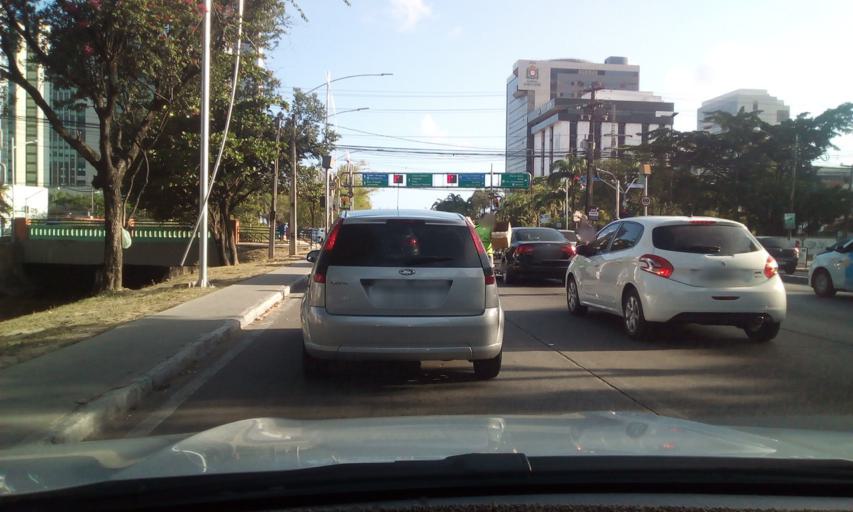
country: BR
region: Pernambuco
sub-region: Recife
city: Recife
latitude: -8.0618
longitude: -34.8978
